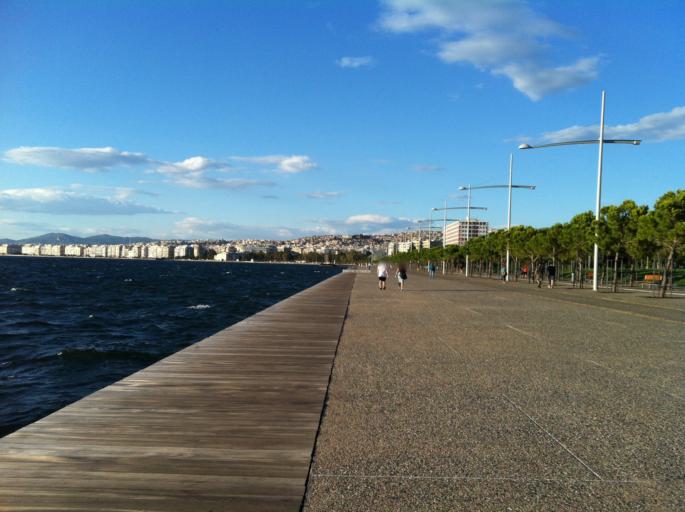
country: GR
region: Central Macedonia
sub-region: Nomos Thessalonikis
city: Triandria
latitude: 40.6135
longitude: 22.9509
